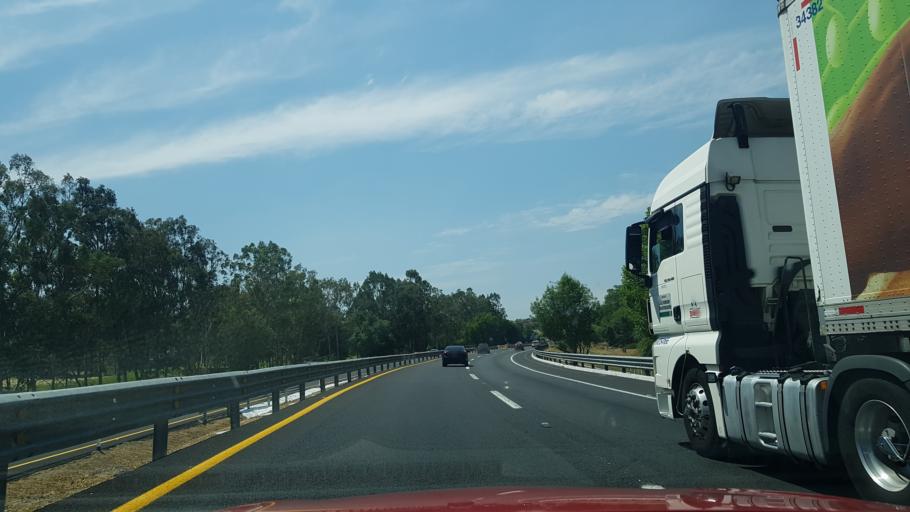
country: MX
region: Michoacan
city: Maravatio
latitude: 19.9034
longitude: -100.4157
